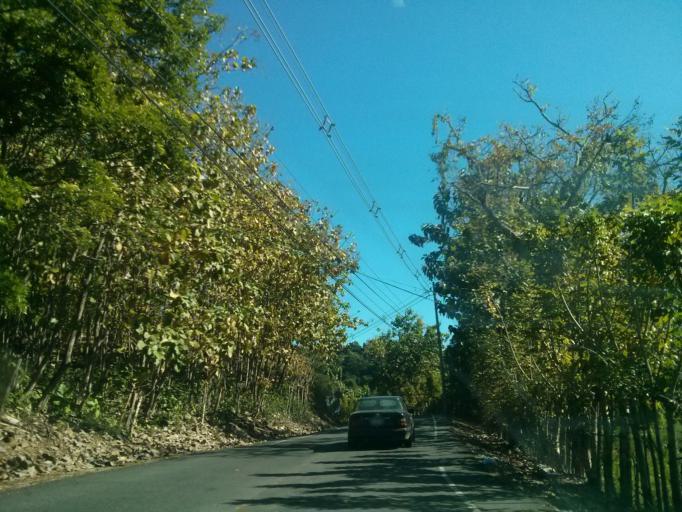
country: CR
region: Puntarenas
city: Paquera
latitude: 9.7858
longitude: -84.9426
